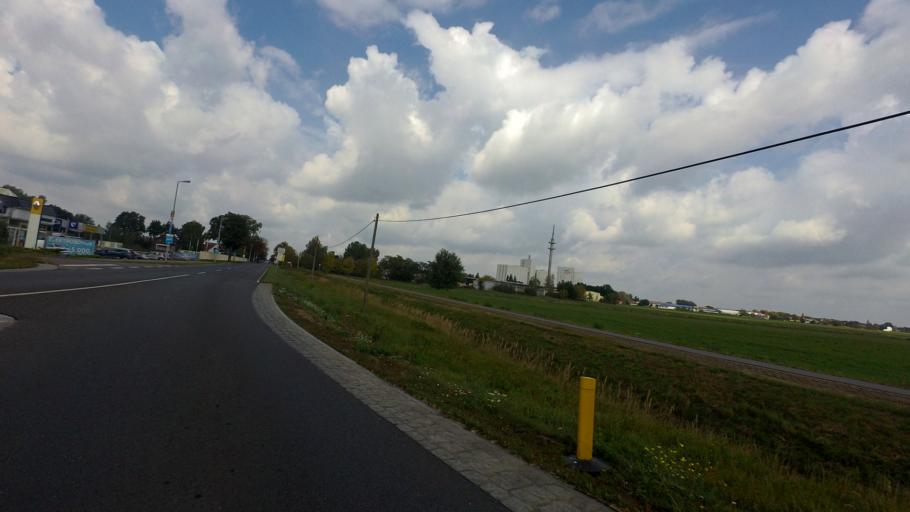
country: DE
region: Brandenburg
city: Herzberg
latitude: 51.6893
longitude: 13.2547
